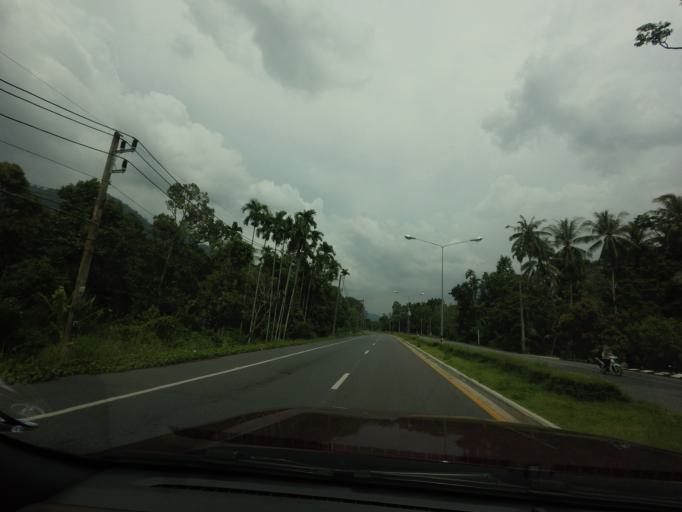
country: TH
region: Yala
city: Krong Pi Nang
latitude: 6.4723
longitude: 101.2667
